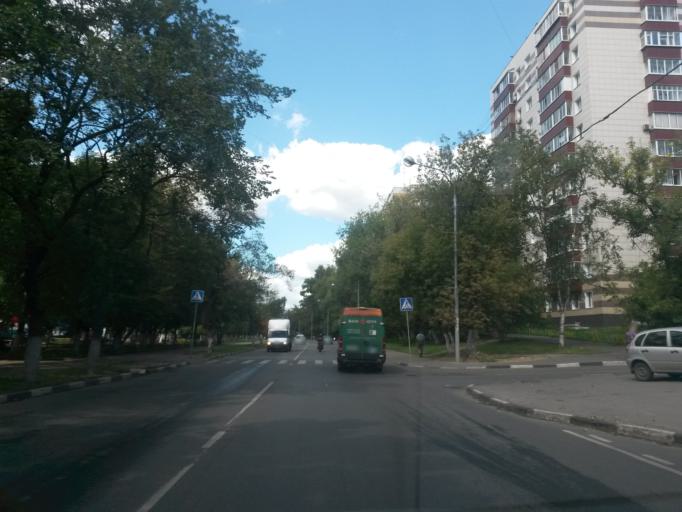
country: RU
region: Moscow
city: Tekstil'shchiki
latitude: 55.6826
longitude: 37.7243
